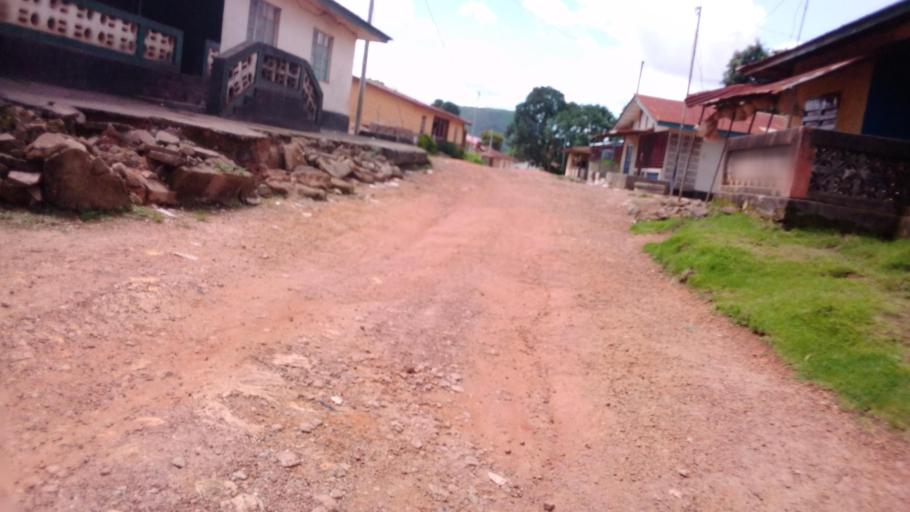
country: SL
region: Northern Province
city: Makeni
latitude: 8.8846
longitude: -12.0359
